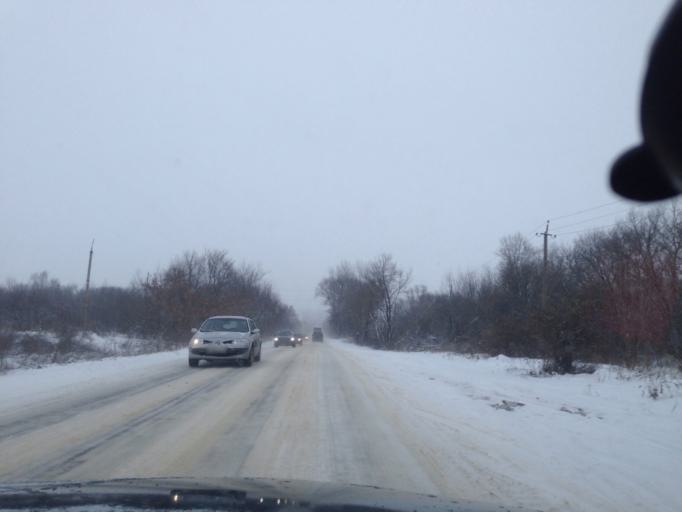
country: RU
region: Tula
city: Bolokhovo
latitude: 54.0825
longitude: 37.8418
